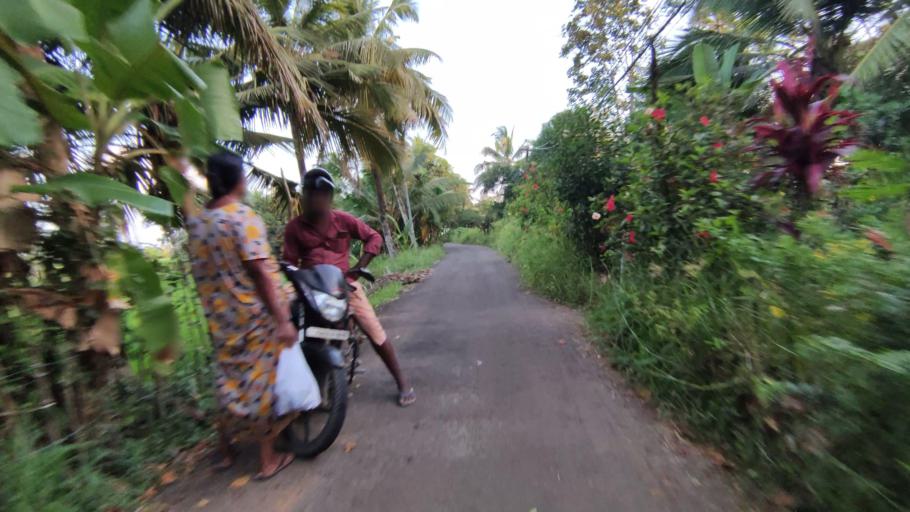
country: IN
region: Kerala
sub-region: Kottayam
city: Kottayam
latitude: 9.5944
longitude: 76.4545
